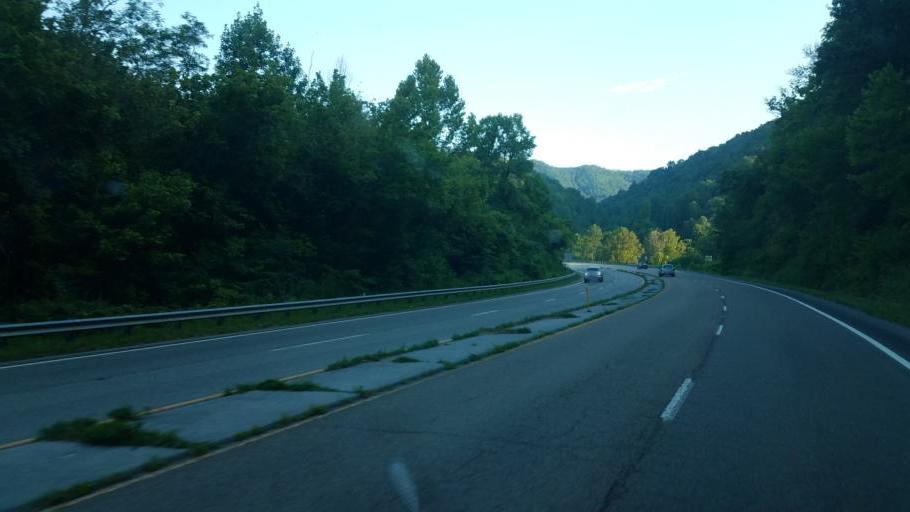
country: US
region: Tennessee
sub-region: Hawkins County
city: Church Hill
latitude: 36.6512
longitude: -82.7490
